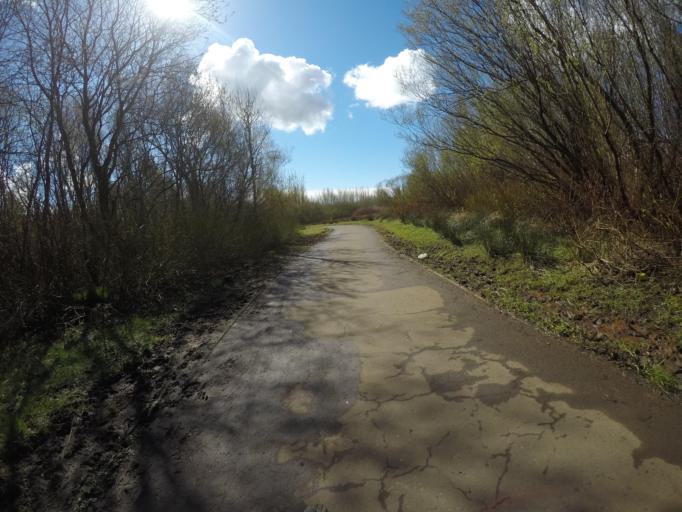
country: GB
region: Scotland
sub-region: North Ayrshire
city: Kilwinning
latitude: 55.6495
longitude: -4.6919
